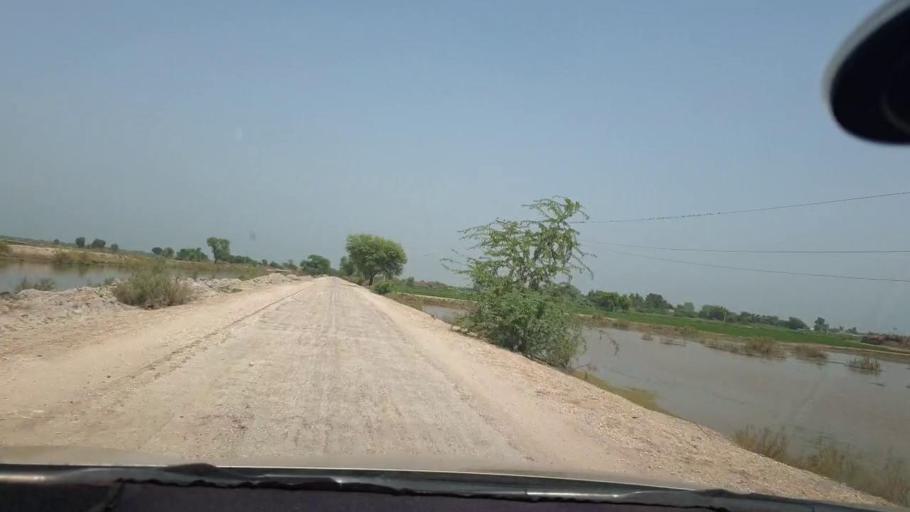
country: PK
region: Sindh
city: Kambar
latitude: 27.6774
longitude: 67.9098
